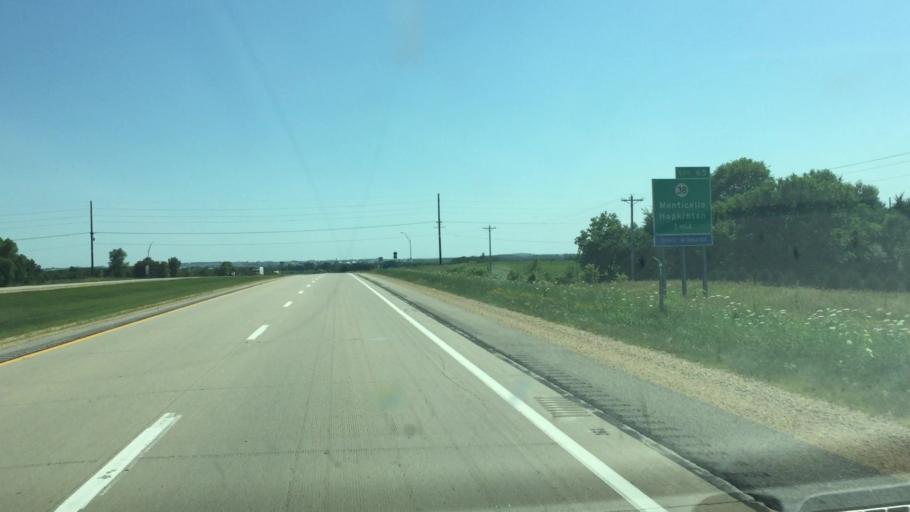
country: US
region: Iowa
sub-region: Jones County
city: Monticello
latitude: 42.2524
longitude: -91.1597
